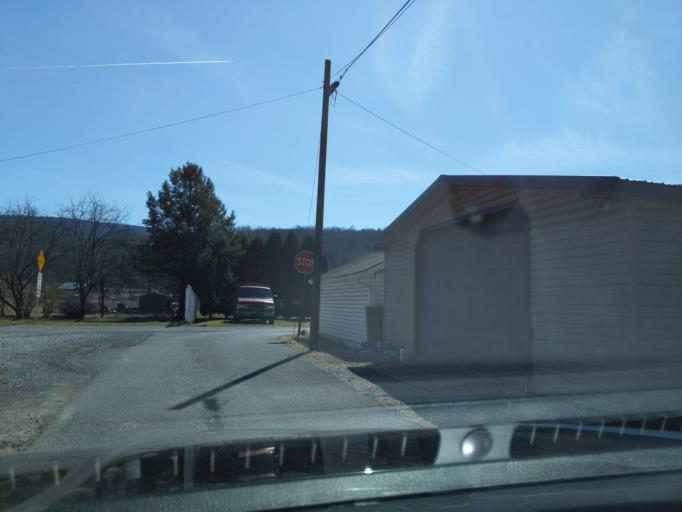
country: US
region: Pennsylvania
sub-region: Blair County
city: Hollidaysburg
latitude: 40.4227
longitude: -78.3936
